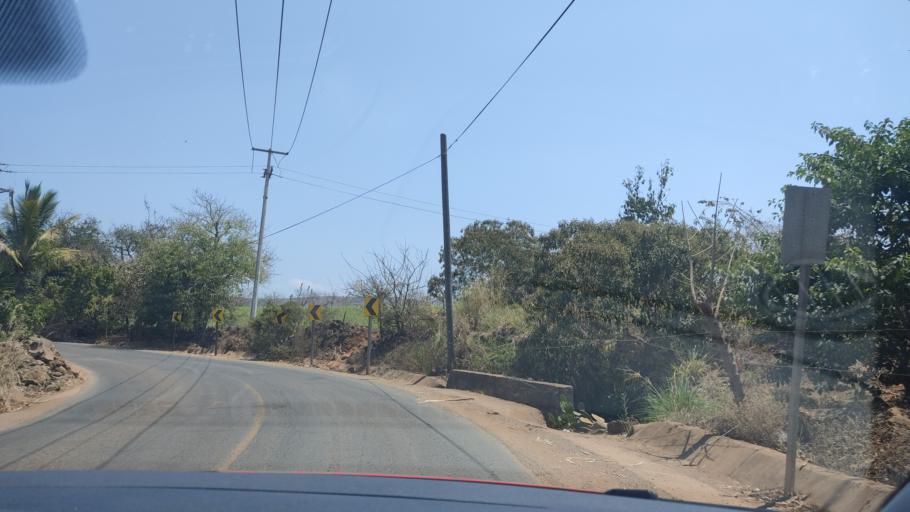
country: MX
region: Nayarit
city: Puga
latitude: 21.5761
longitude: -104.7834
